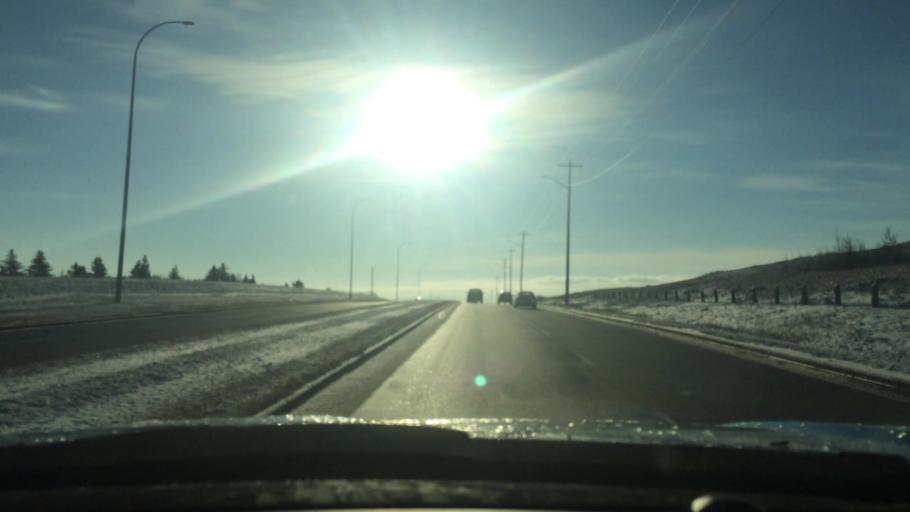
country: CA
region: Alberta
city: Calgary
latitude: 51.1215
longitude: -114.0922
